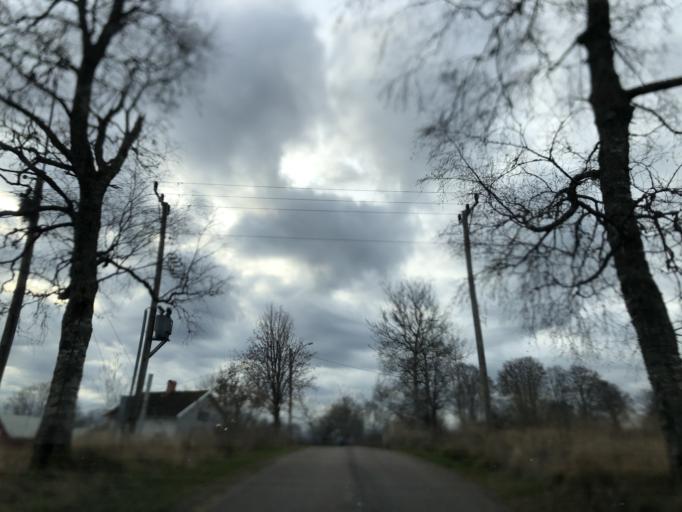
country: SE
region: Vaestra Goetaland
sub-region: Ulricehamns Kommun
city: Ulricehamn
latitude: 57.7299
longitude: 13.3176
